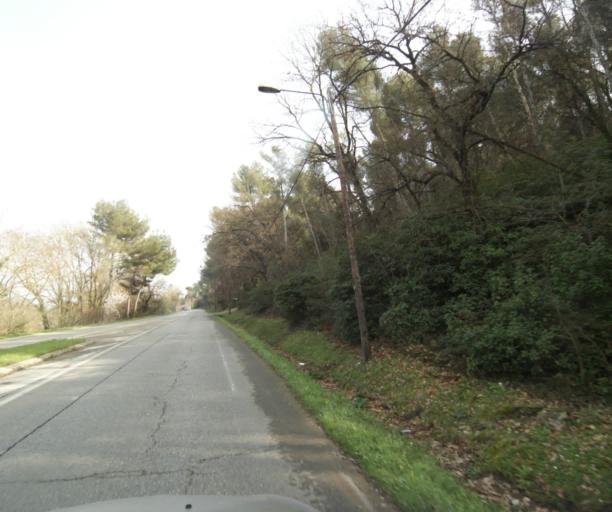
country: FR
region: Provence-Alpes-Cote d'Azur
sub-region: Departement des Bouches-du-Rhone
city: Les Pennes-Mirabeau
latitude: 43.4079
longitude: 5.3051
